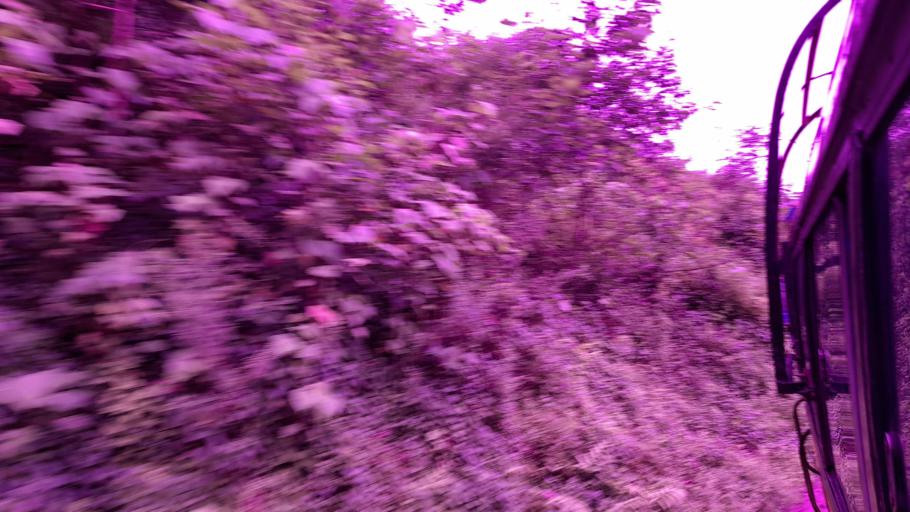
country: NP
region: Central Region
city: Kirtipur
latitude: 27.8258
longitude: 85.2090
